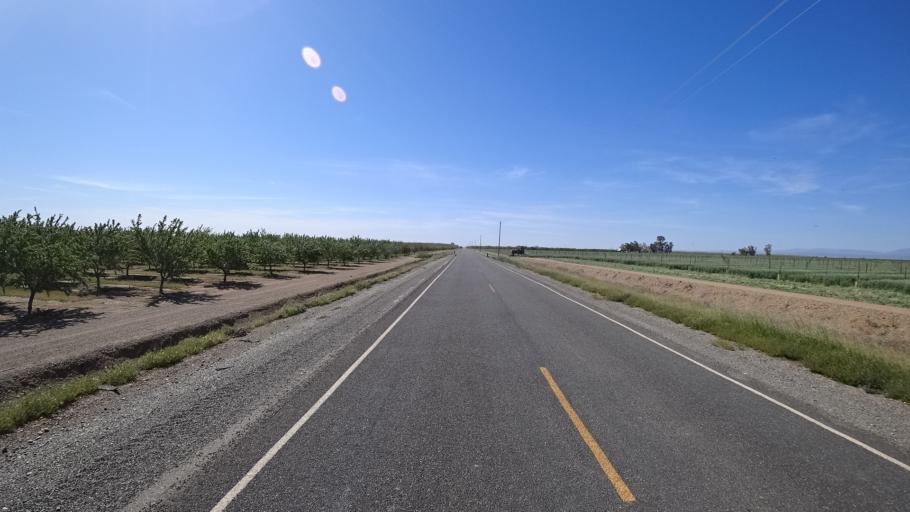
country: US
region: California
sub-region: Glenn County
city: Hamilton City
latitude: 39.6439
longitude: -122.1038
